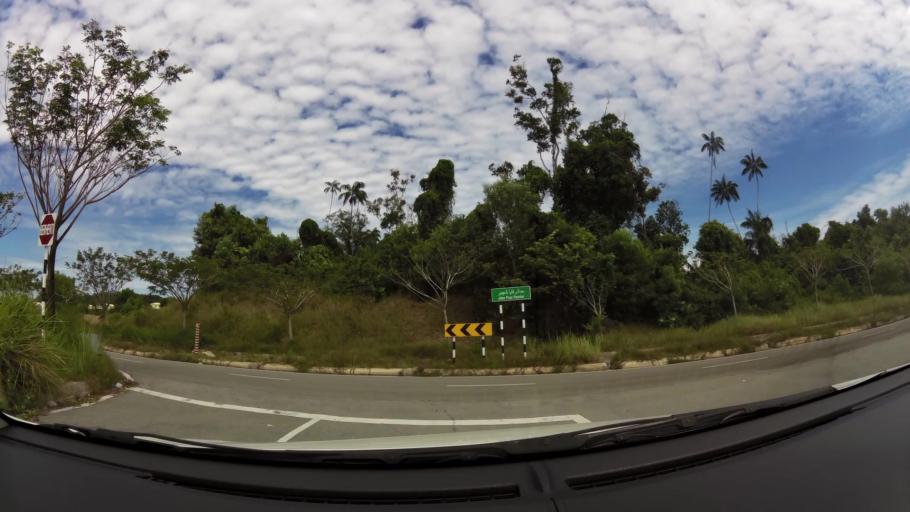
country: BN
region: Brunei and Muara
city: Bandar Seri Begawan
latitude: 4.9876
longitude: 115.0166
